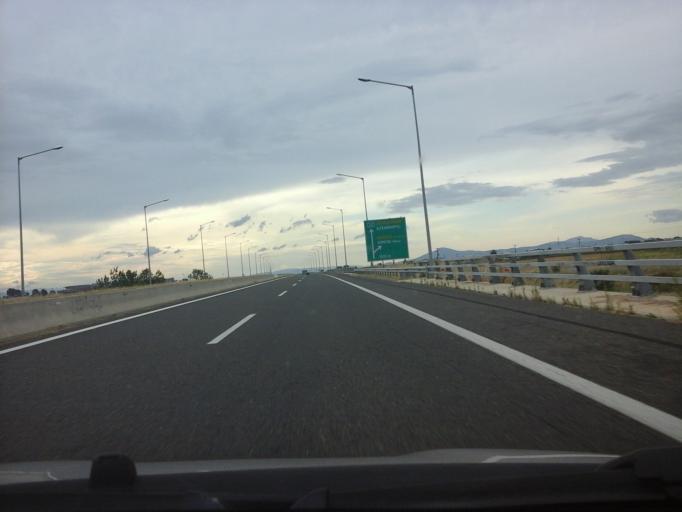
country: GR
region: East Macedonia and Thrace
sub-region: Nomos Rodopis
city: Komotini
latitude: 41.1089
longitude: 25.3409
